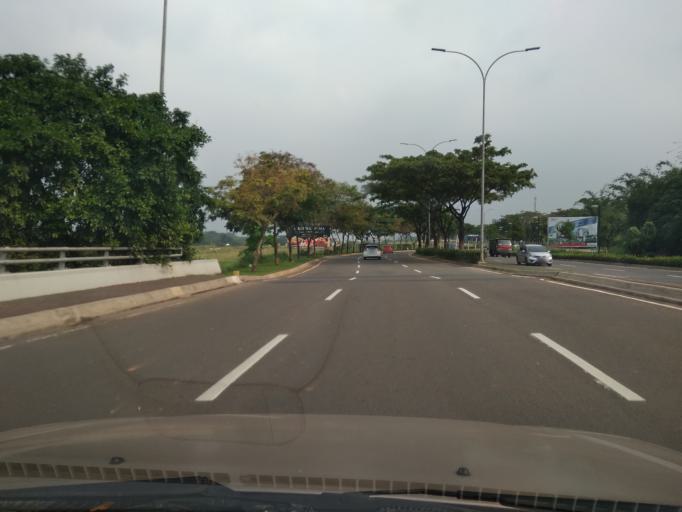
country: ID
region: West Java
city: Serpong
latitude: -6.2860
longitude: 106.6544
